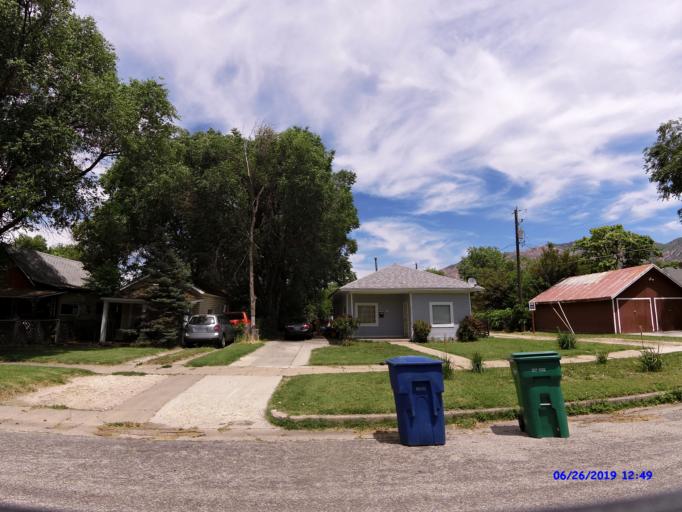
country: US
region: Utah
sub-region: Weber County
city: Ogden
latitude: 41.2268
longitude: -111.9572
